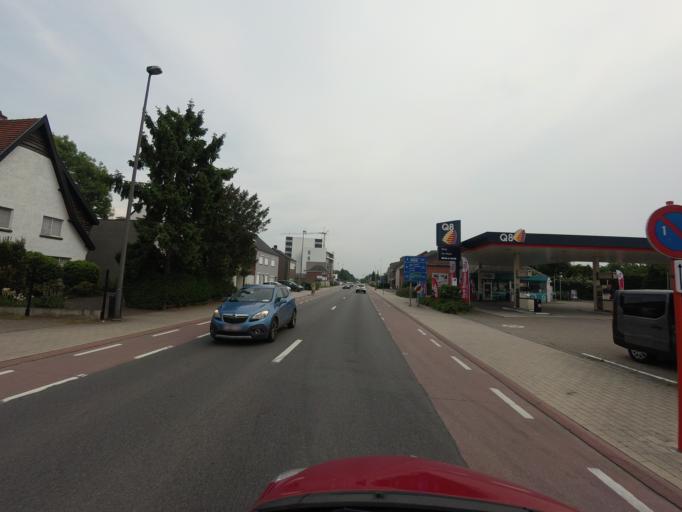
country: BE
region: Flanders
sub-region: Provincie Limburg
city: Lommel
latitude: 51.2239
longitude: 5.3141
